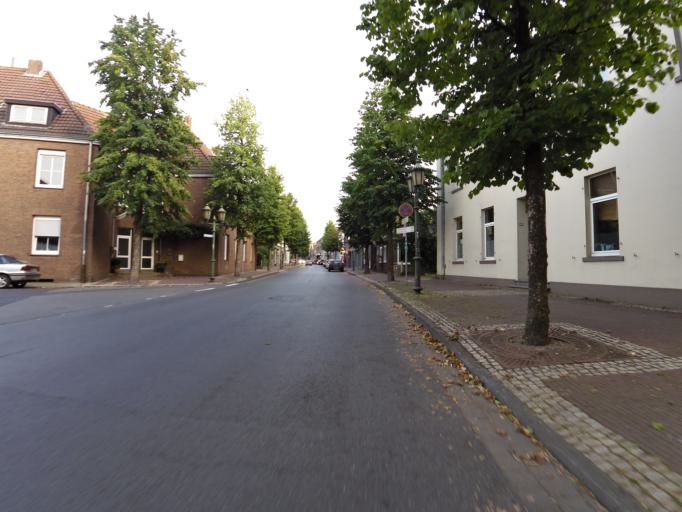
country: DE
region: North Rhine-Westphalia
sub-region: Regierungsbezirk Dusseldorf
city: Kleve
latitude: 51.8740
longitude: 6.1565
